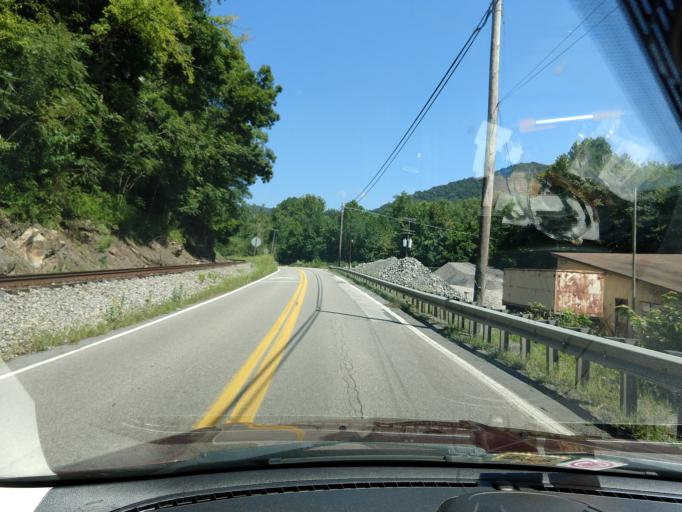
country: US
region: West Virginia
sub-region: Fayette County
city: Ansted
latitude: 38.1418
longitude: -81.2120
